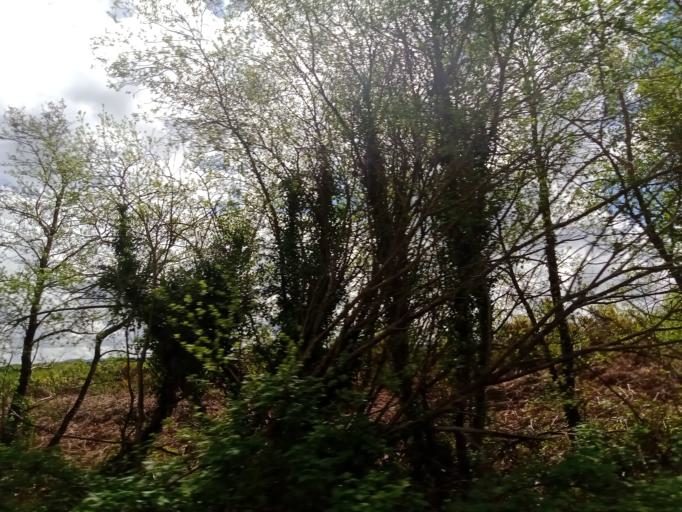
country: IE
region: Munster
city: Thurles
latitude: 52.6829
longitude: -7.6613
